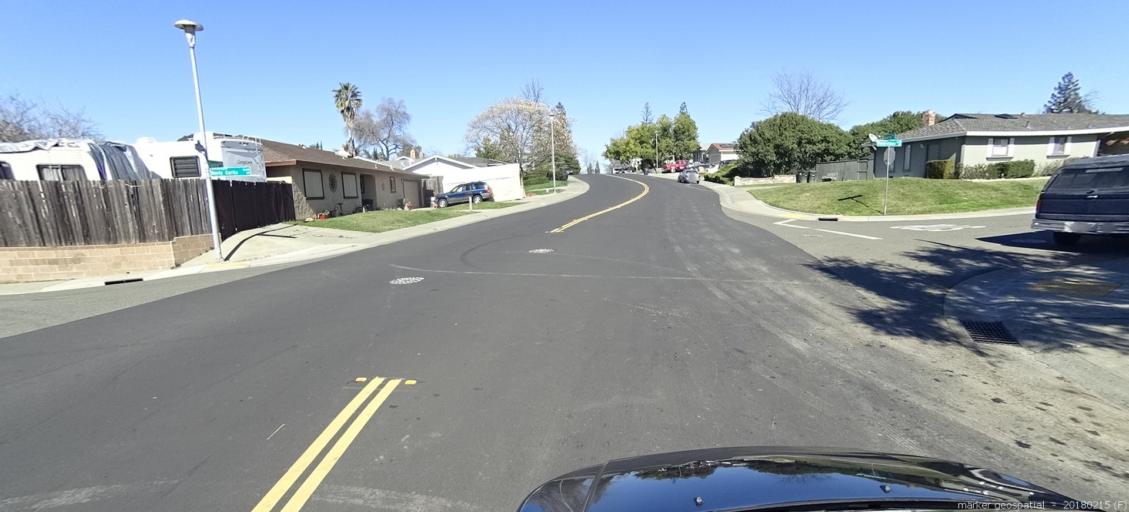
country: US
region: California
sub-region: Sacramento County
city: Fair Oaks
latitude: 38.6681
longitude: -121.2982
